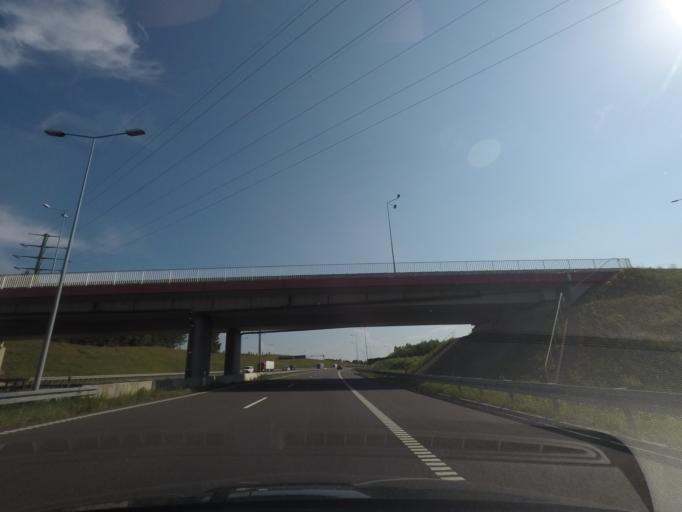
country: PL
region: Silesian Voivodeship
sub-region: Powiat rybnicki
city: Swierklany Gorne
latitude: 50.0259
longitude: 18.6021
